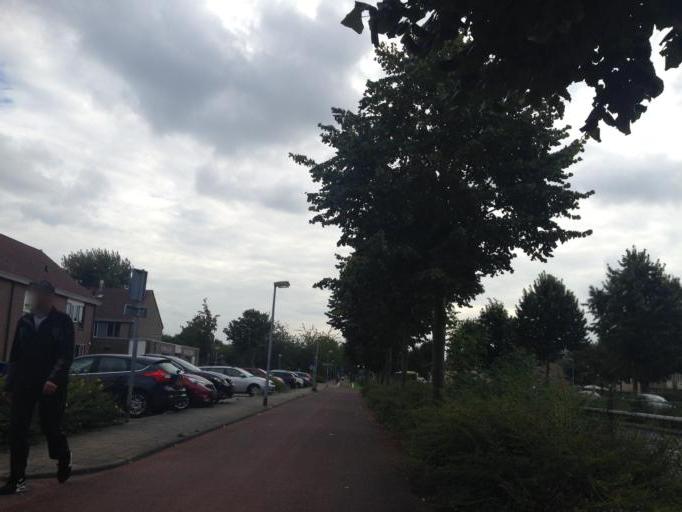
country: NL
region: Flevoland
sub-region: Gemeente Almere
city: Almere Stad
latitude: 52.4007
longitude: 5.2694
